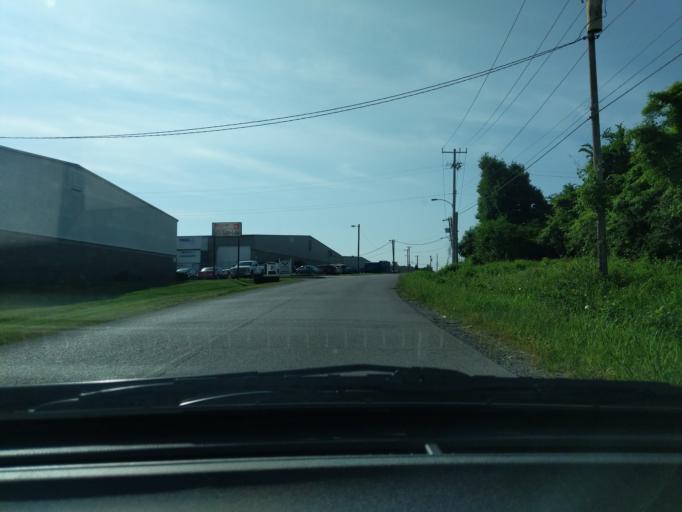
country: US
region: Tennessee
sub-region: Davidson County
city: Oak Hill
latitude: 36.0942
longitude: -86.6947
